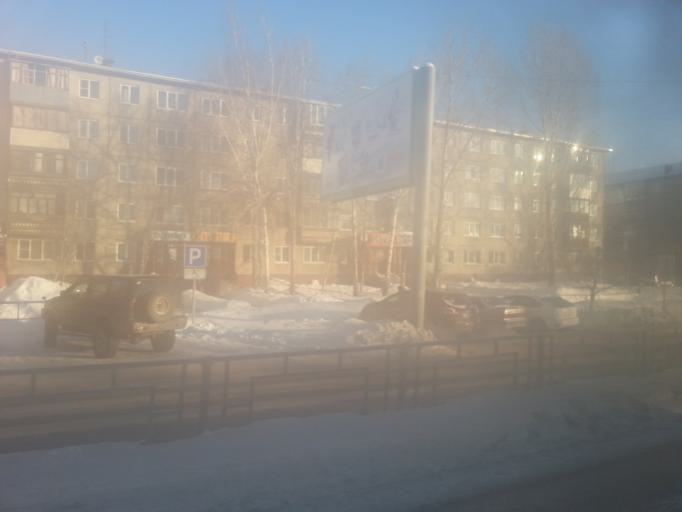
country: RU
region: Altai Krai
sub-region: Gorod Barnaulskiy
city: Barnaul
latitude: 53.3589
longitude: 83.7035
